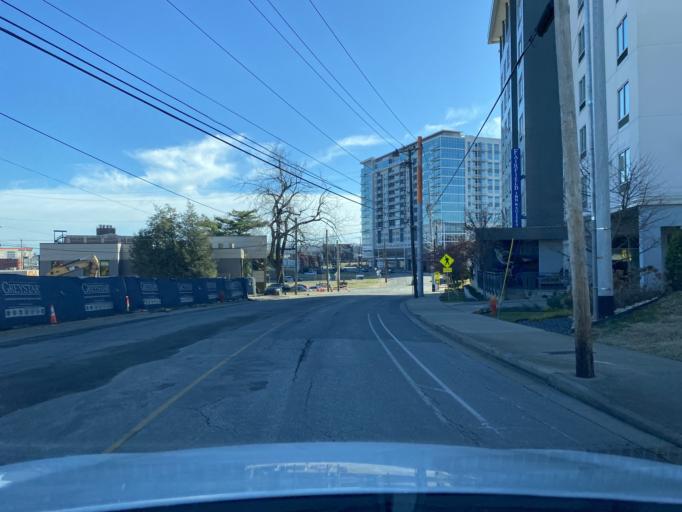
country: US
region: Tennessee
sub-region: Davidson County
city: Nashville
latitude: 36.1507
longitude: -86.7818
